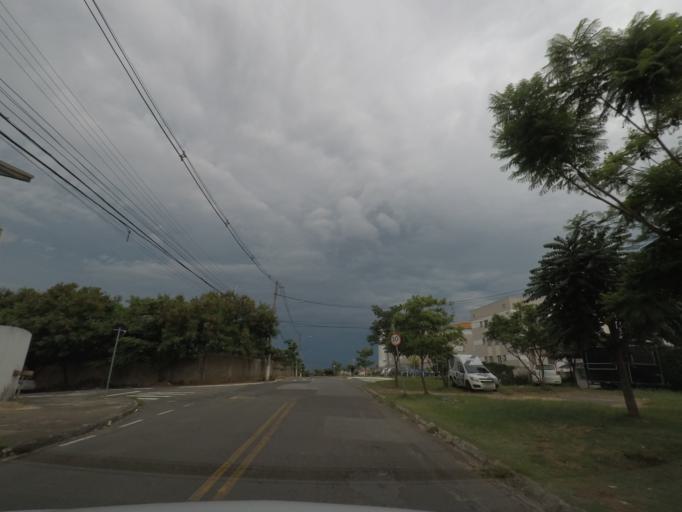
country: BR
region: Sao Paulo
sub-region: Campinas
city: Campinas
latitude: -22.9303
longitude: -47.1235
